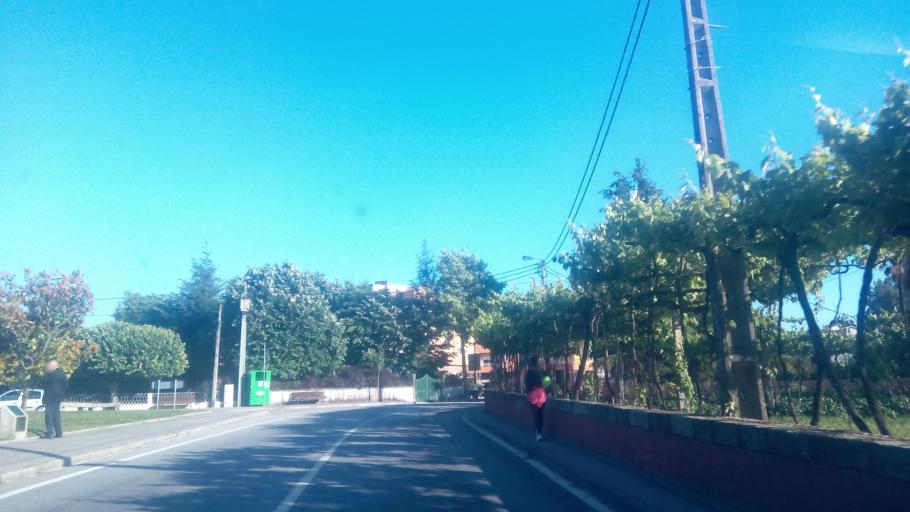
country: PT
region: Porto
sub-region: Paredes
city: Madalena
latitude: 41.2294
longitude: -8.3623
